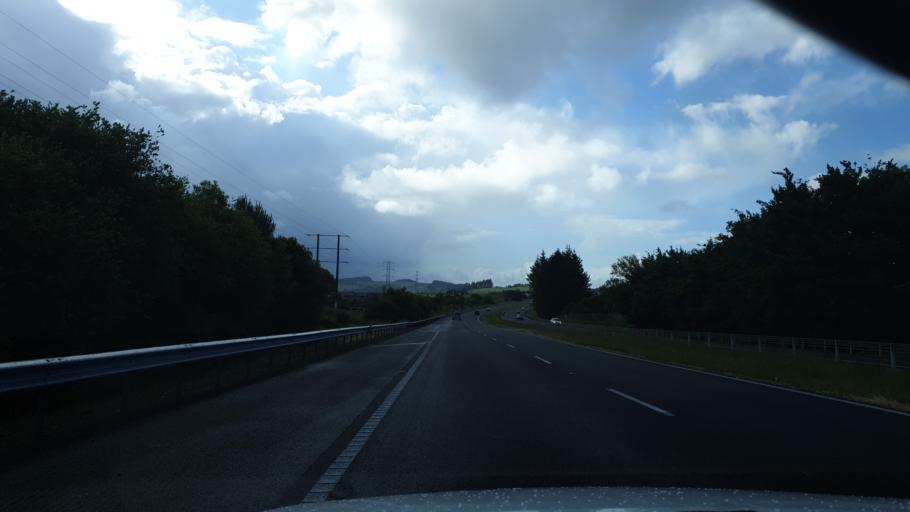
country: NZ
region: Auckland
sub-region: Auckland
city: Pukekohe East
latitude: -37.2409
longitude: 175.0226
